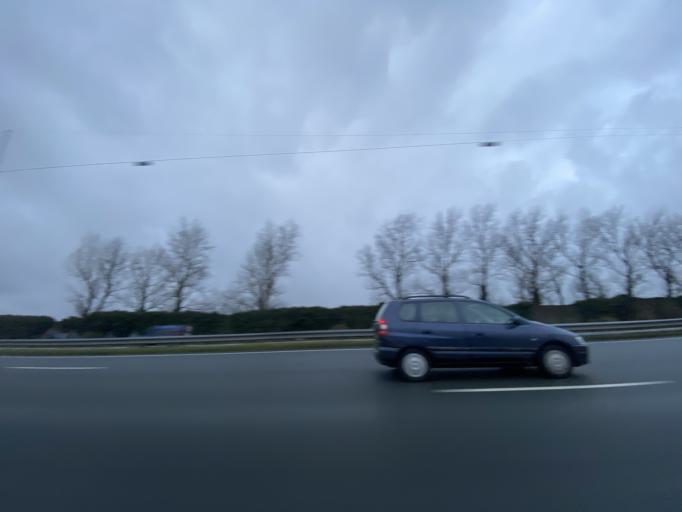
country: NL
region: North Holland
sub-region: Gemeente Uitgeest
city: Uitgeest
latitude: 52.5123
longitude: 4.7114
